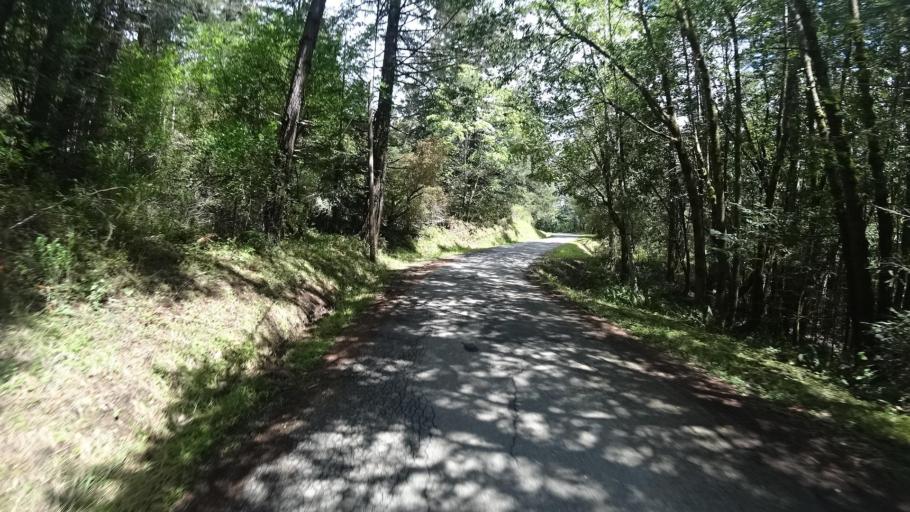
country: US
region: California
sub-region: Humboldt County
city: Blue Lake
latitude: 40.7660
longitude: -123.9472
